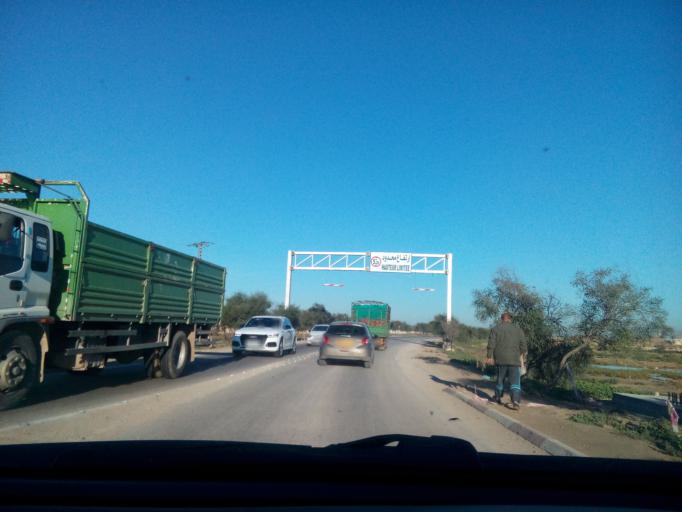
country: DZ
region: Relizane
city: Relizane
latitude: 35.7870
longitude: 0.5285
